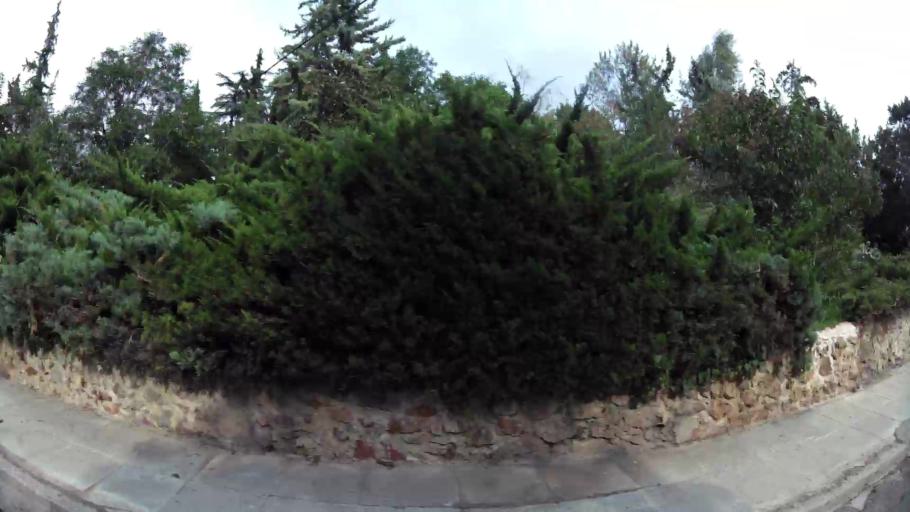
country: GR
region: Attica
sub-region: Nomarchia Athinas
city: Filothei
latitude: 38.0276
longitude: 23.7797
